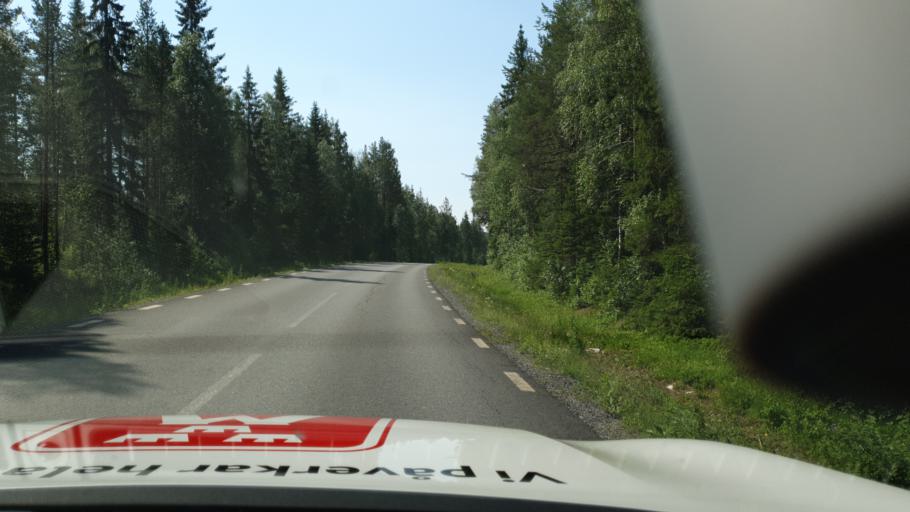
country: SE
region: Vaesterbotten
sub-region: Skelleftea Kommun
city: Langsele
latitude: 64.9624
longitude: 20.0439
